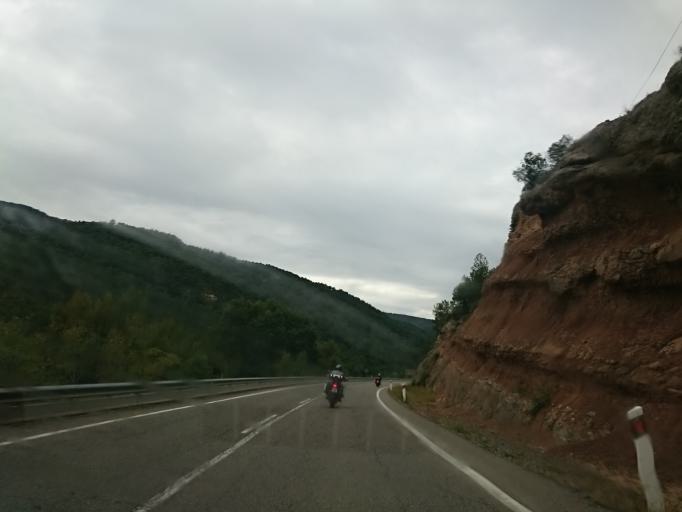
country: ES
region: Catalonia
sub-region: Provincia de Lleida
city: Senterada
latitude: 42.2647
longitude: 1.0190
